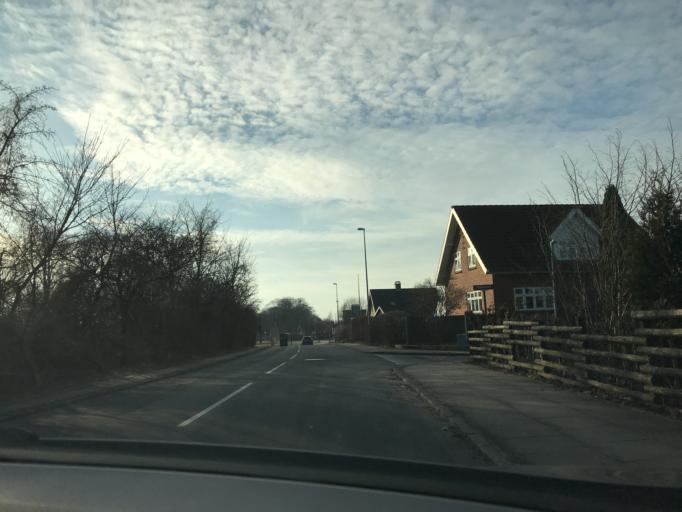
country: DK
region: South Denmark
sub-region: Vejle Kommune
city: Vejle
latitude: 55.7154
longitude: 9.5627
